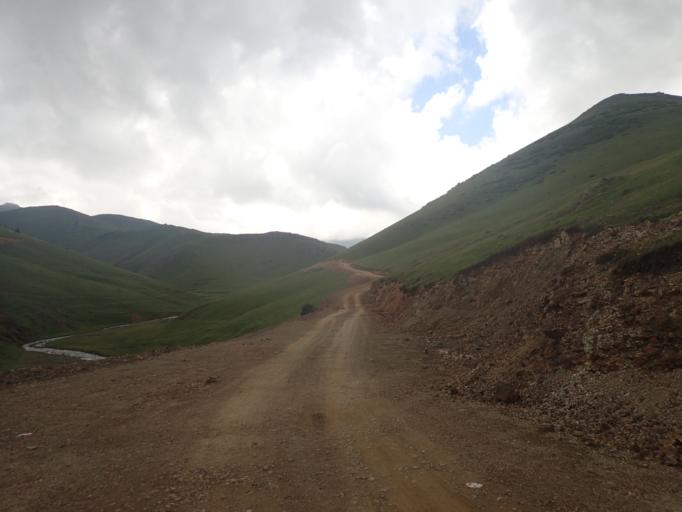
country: TR
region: Ordu
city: Yesilce
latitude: 40.5869
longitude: 37.9635
